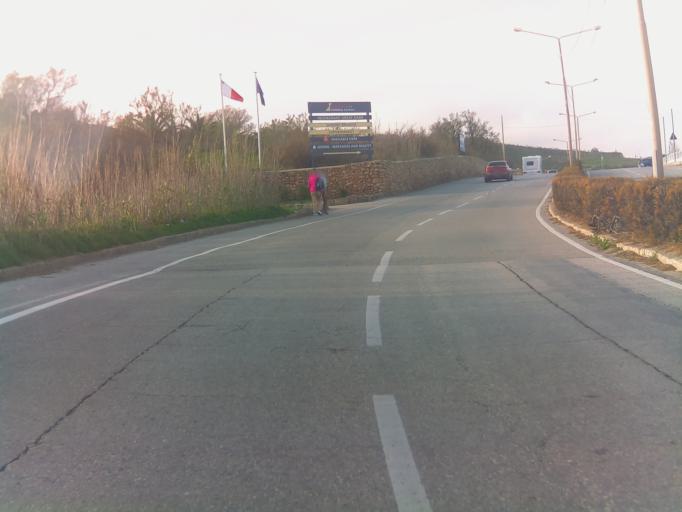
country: MT
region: Il-Mellieha
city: Mellieha
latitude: 35.9665
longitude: 14.3522
